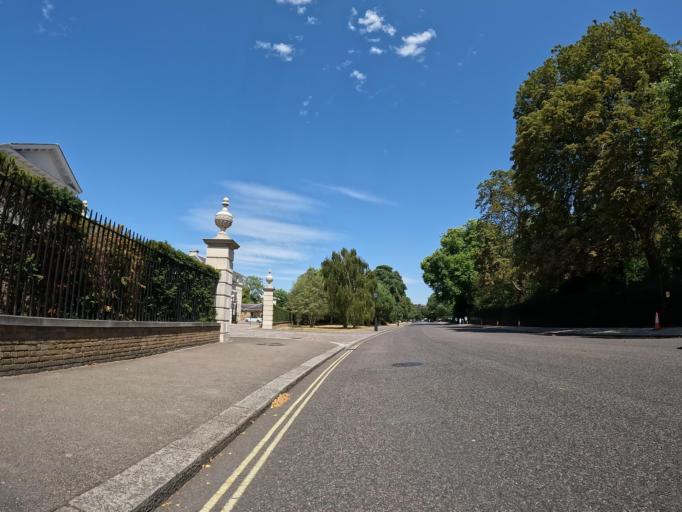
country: GB
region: England
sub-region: Greater London
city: Belsize Park
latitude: 51.5313
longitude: -0.1653
